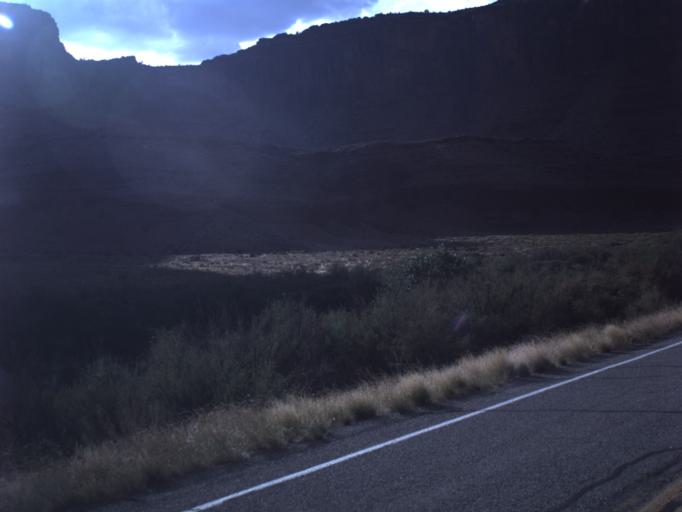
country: US
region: Utah
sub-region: Grand County
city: Moab
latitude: 38.7763
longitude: -109.3291
